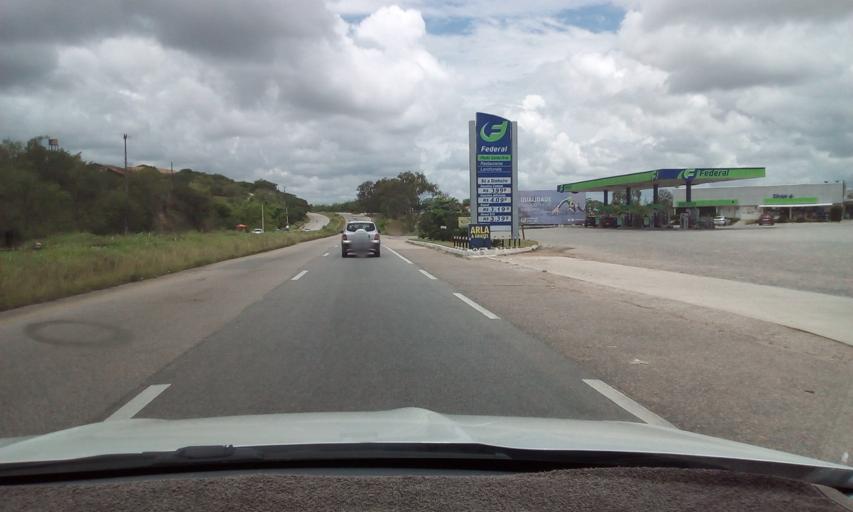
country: BR
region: Pernambuco
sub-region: Gravata
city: Gravata
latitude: -8.1909
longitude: -35.5100
